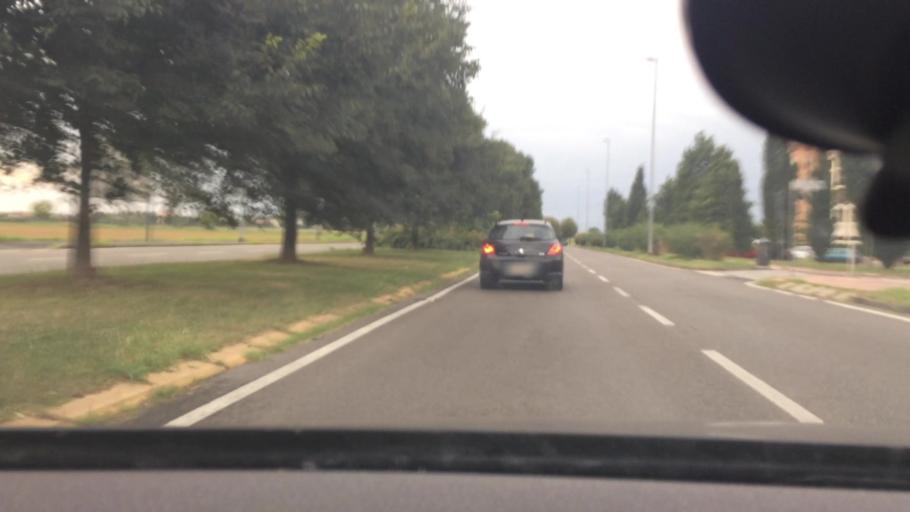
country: IT
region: Lombardy
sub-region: Citta metropolitana di Milano
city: Cusano Milanino
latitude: 45.5607
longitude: 9.1982
